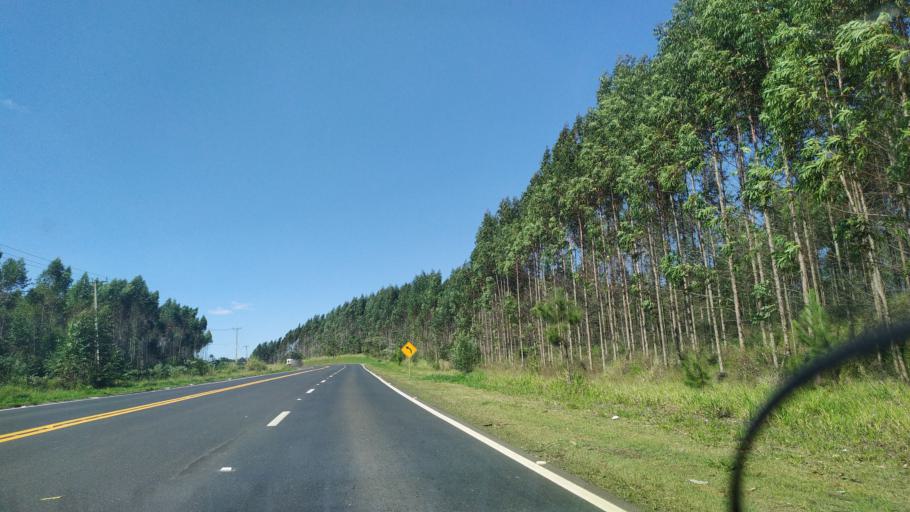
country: BR
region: Parana
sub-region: Telemaco Borba
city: Telemaco Borba
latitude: -24.3069
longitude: -50.6954
